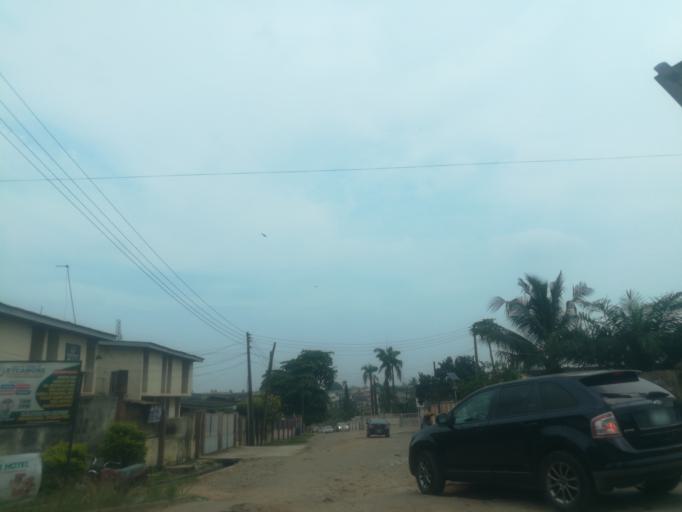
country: NG
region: Oyo
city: Ibadan
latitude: 7.4223
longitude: 3.9141
